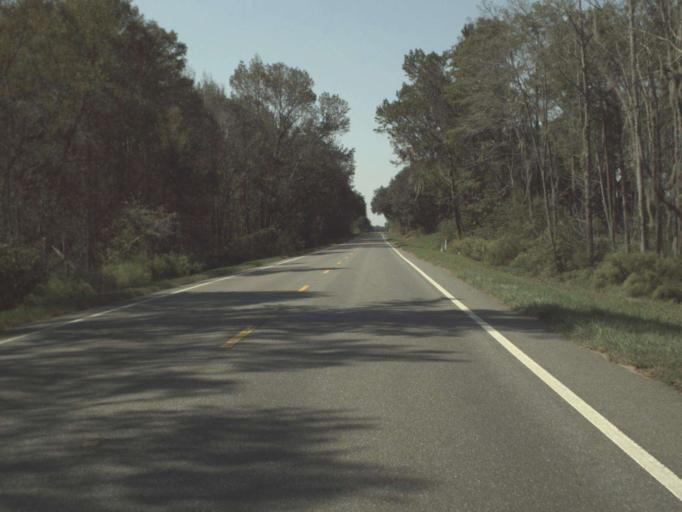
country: US
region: Florida
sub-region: Jackson County
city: Malone
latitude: 30.9591
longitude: -85.1869
